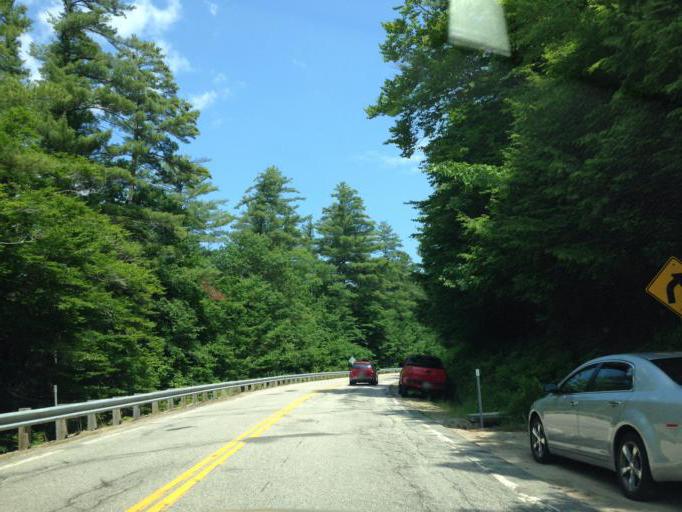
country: US
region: New Hampshire
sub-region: Carroll County
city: Conway
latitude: 43.9910
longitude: -71.1717
